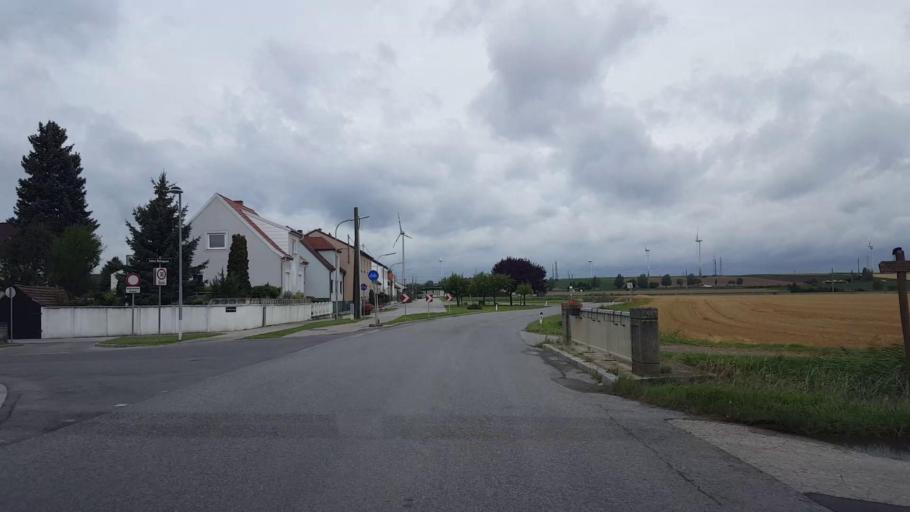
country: AT
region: Lower Austria
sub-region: Politischer Bezirk Bruck an der Leitha
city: Bruck an der Leitha
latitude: 48.0194
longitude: 16.7200
